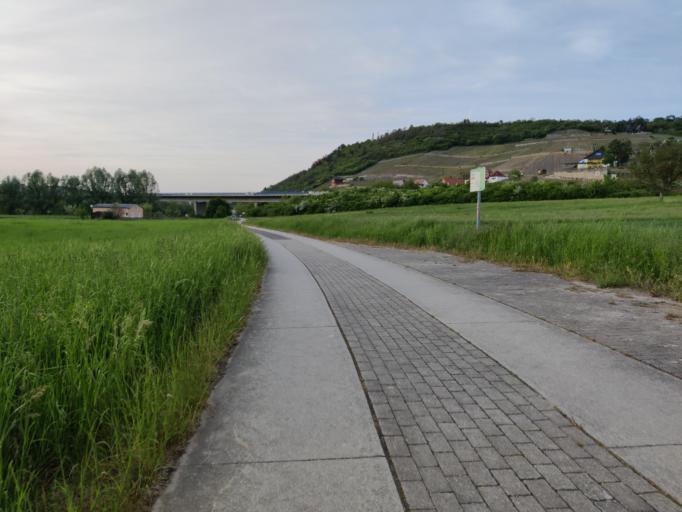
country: DE
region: Saxony-Anhalt
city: Freyburg
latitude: 51.1997
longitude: 11.7768
